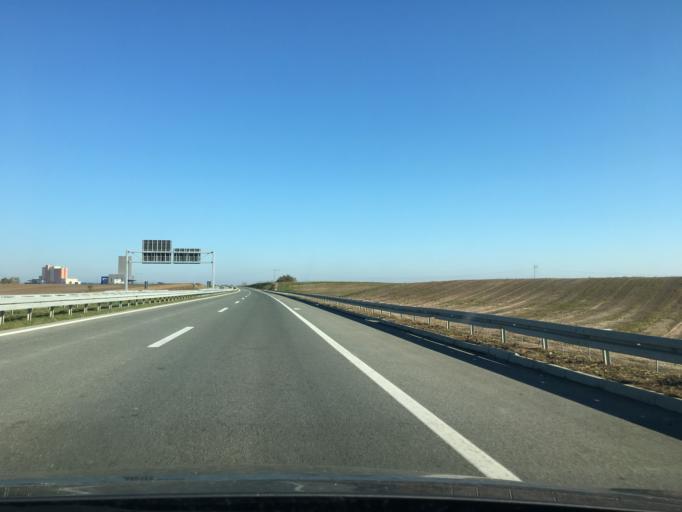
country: RS
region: Autonomna Pokrajina Vojvodina
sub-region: Severnobacki Okrug
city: Mali Igos
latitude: 45.6484
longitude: 19.7188
